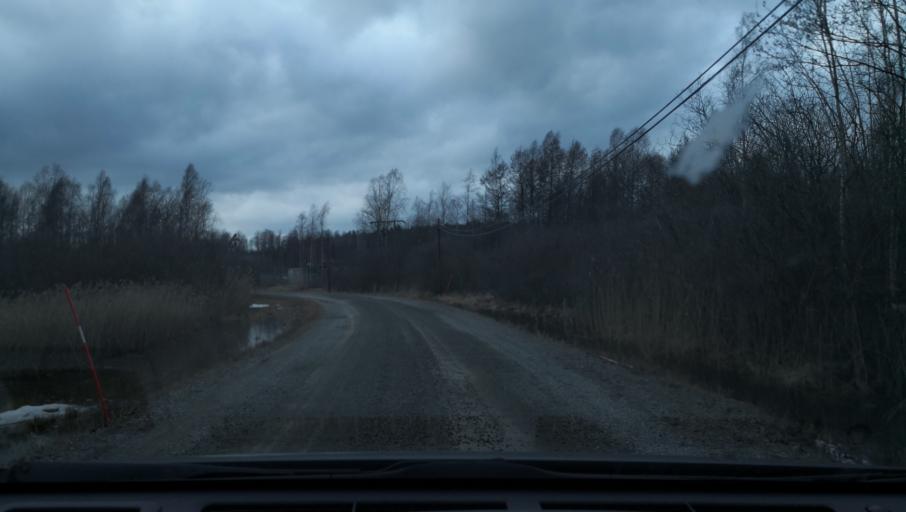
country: SE
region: Vaestmanland
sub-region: Kopings Kommun
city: Kolsva
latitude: 59.5989
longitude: 15.7128
